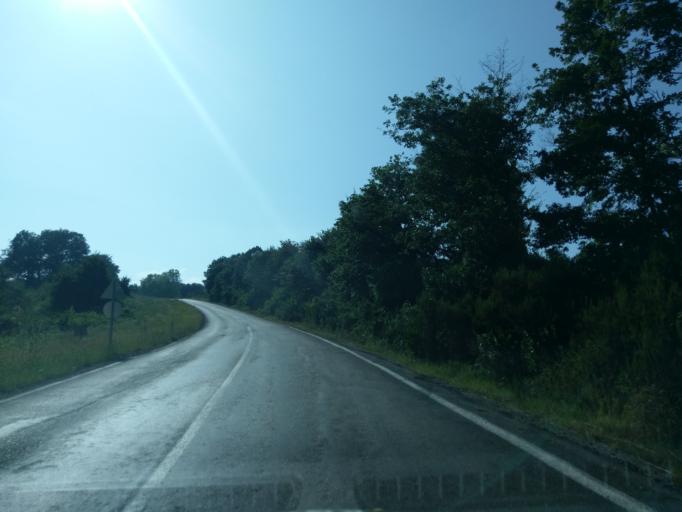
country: TR
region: Sinop
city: Erfelek
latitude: 41.9501
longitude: 34.7672
